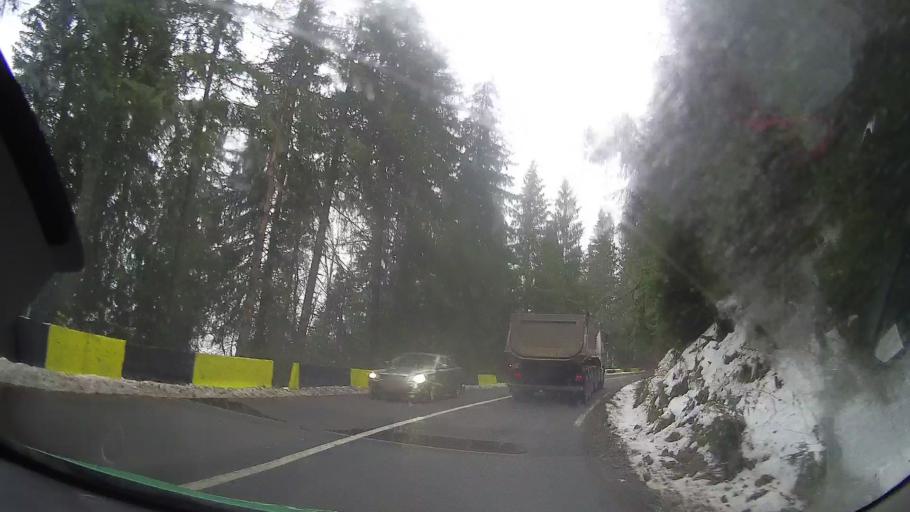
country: RO
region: Harghita
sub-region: Oras Balan
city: Balan
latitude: 46.7775
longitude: 25.7436
